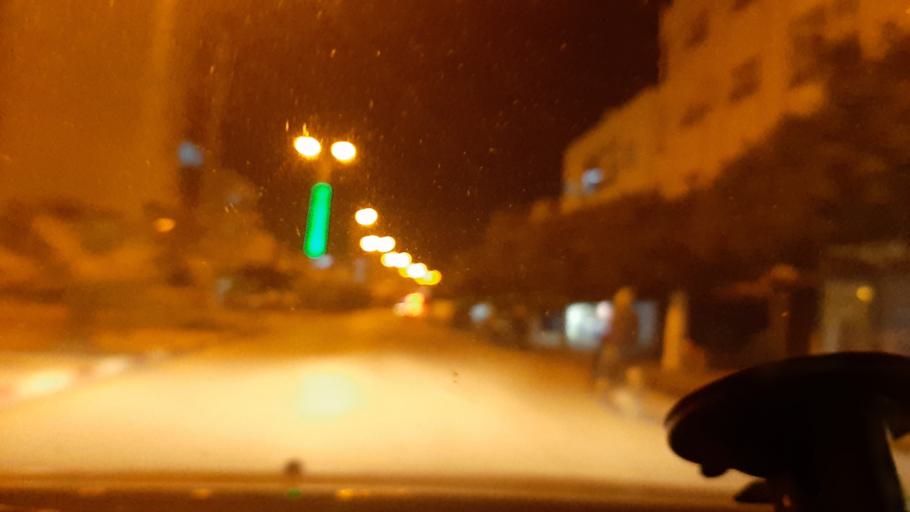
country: TN
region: Safaqis
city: Sfax
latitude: 34.7331
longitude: 10.7574
